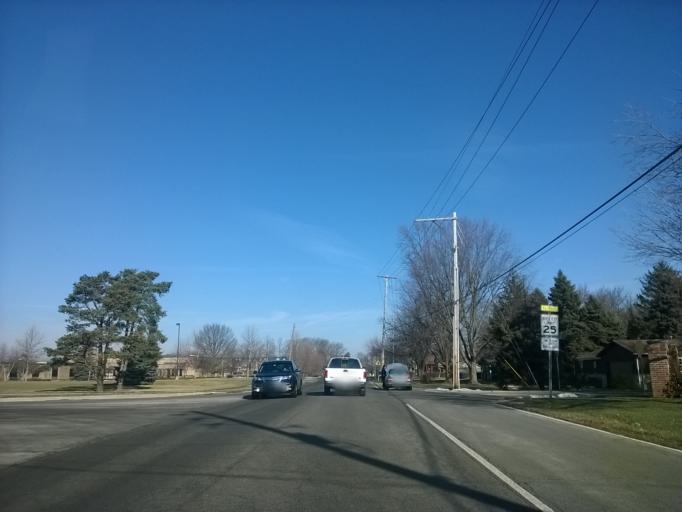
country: US
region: Indiana
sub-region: Hamilton County
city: Carmel
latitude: 39.9726
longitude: -86.1410
